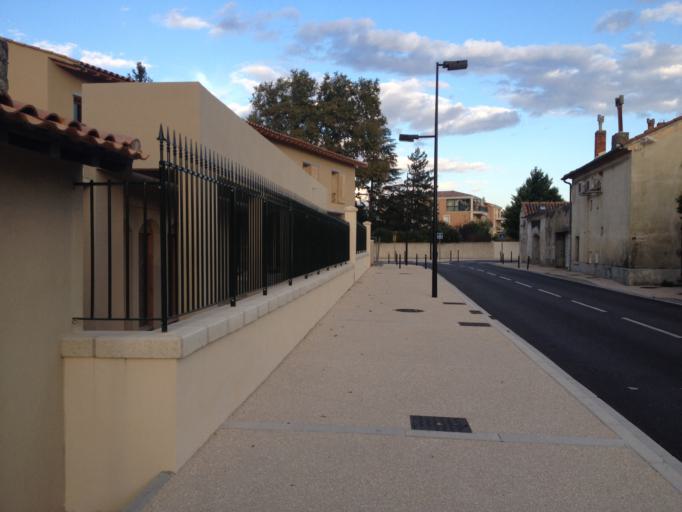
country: FR
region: Provence-Alpes-Cote d'Azur
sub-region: Departement du Vaucluse
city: Orange
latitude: 44.1418
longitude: 4.8072
